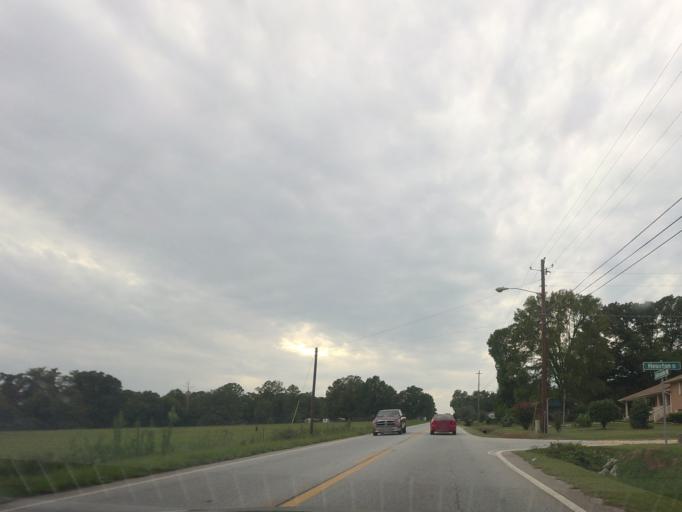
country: US
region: Georgia
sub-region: Bibb County
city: Macon
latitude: 32.8055
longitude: -83.5055
